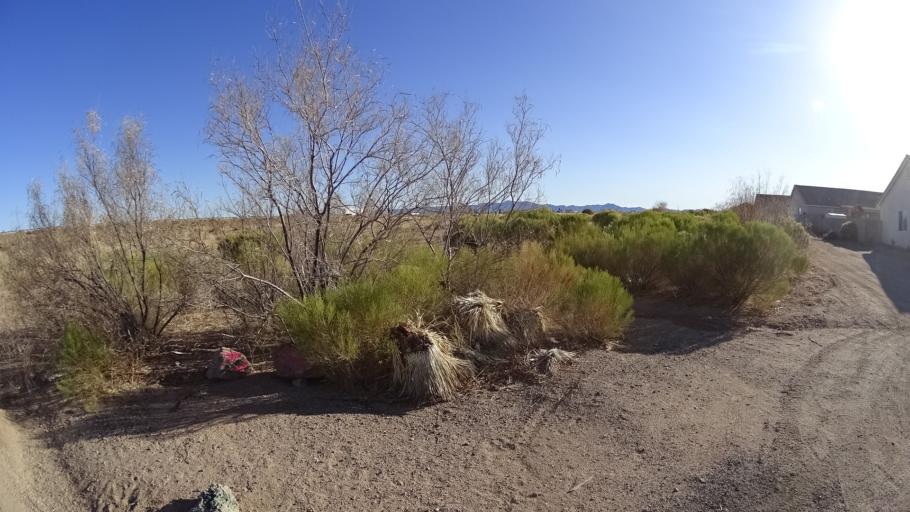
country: US
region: Arizona
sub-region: Mohave County
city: Kingman
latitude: 35.2154
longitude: -114.0052
